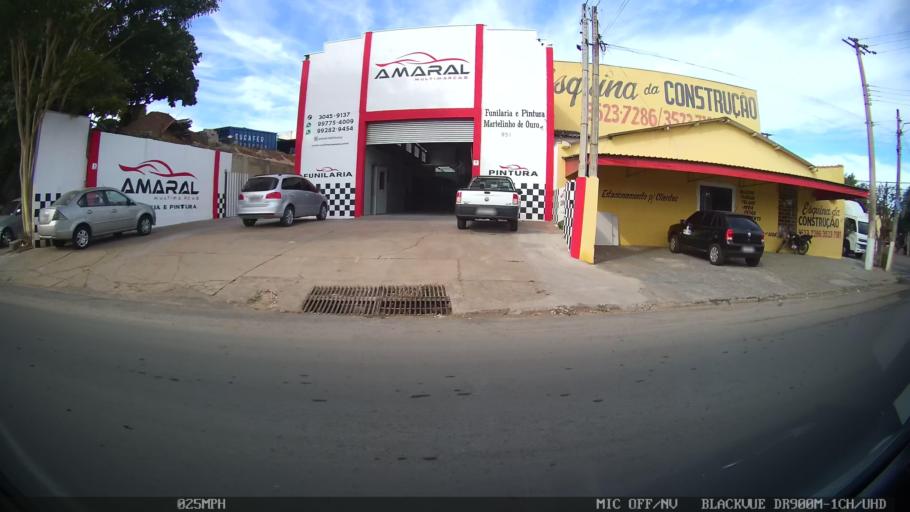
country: BR
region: Sao Paulo
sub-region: Catanduva
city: Catanduva
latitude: -21.1382
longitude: -48.9981
